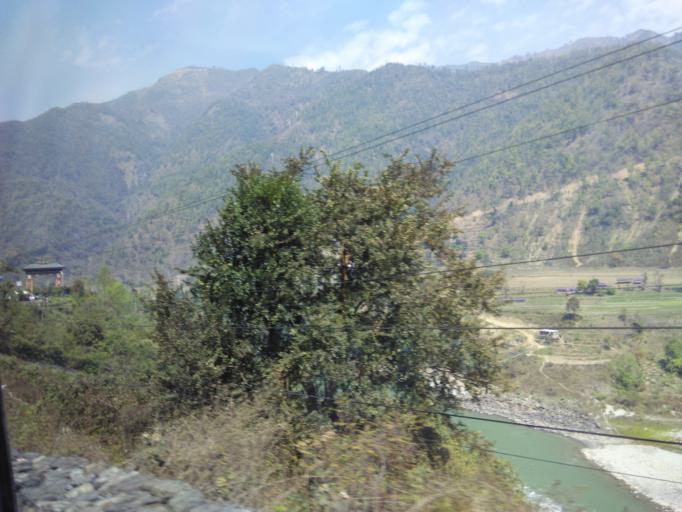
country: NP
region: Central Region
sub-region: Narayani Zone
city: Bharatpur
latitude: 27.8761
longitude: 84.5934
